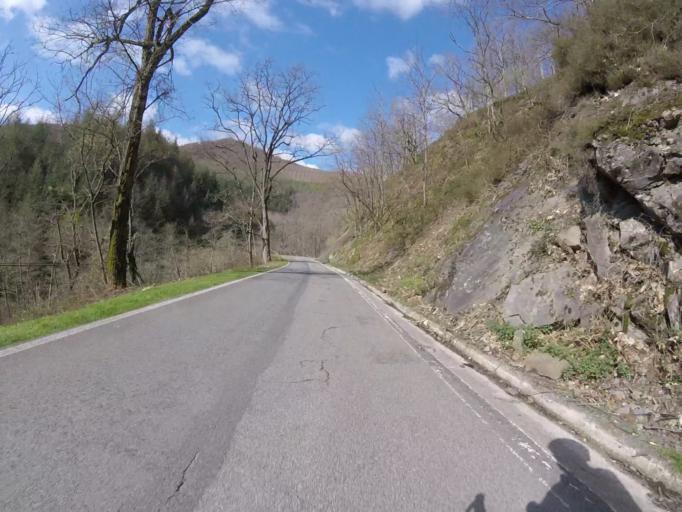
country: ES
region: Navarre
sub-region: Provincia de Navarra
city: Goizueta
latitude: 43.1551
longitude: -1.8478
